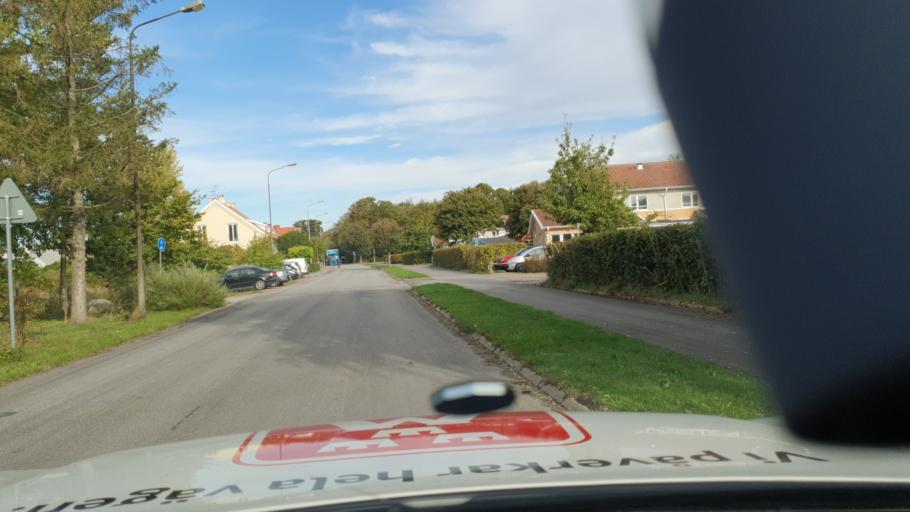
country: SE
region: Skane
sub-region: Malmo
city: Bunkeflostrand
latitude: 55.5220
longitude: 12.9324
